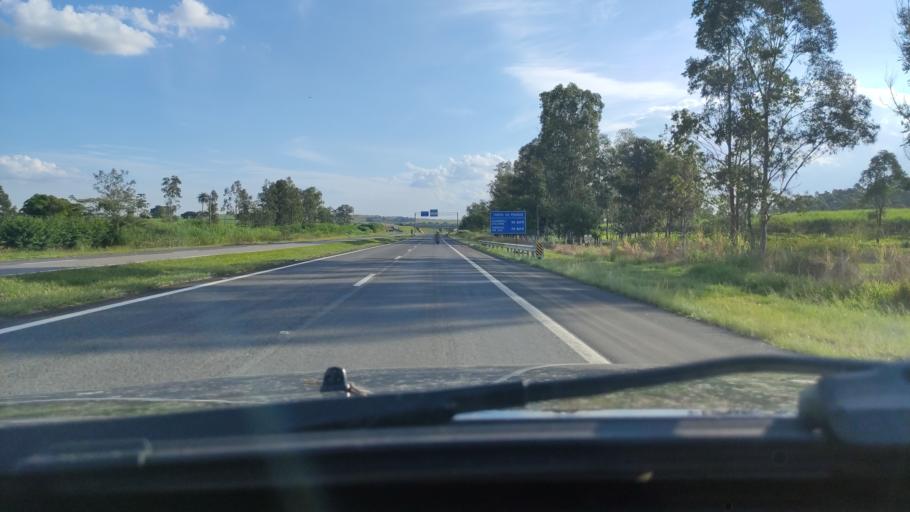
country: BR
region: Sao Paulo
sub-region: Mogi-Mirim
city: Mogi Mirim
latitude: -22.4521
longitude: -46.8915
